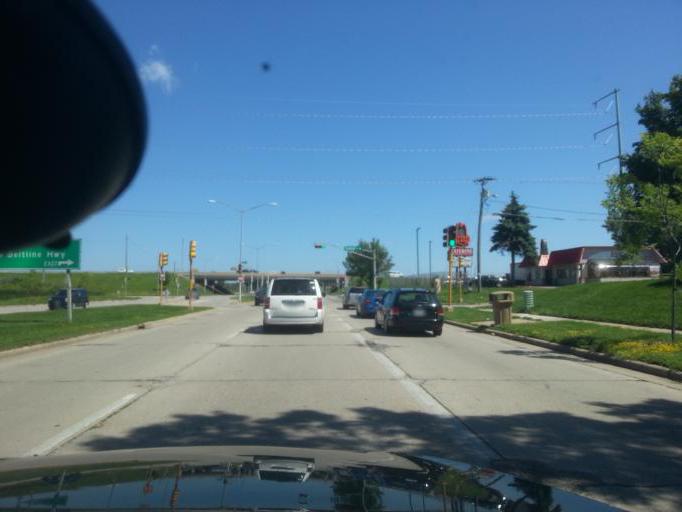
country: US
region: Wisconsin
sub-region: Dane County
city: Middleton
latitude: 43.0513
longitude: -89.5030
